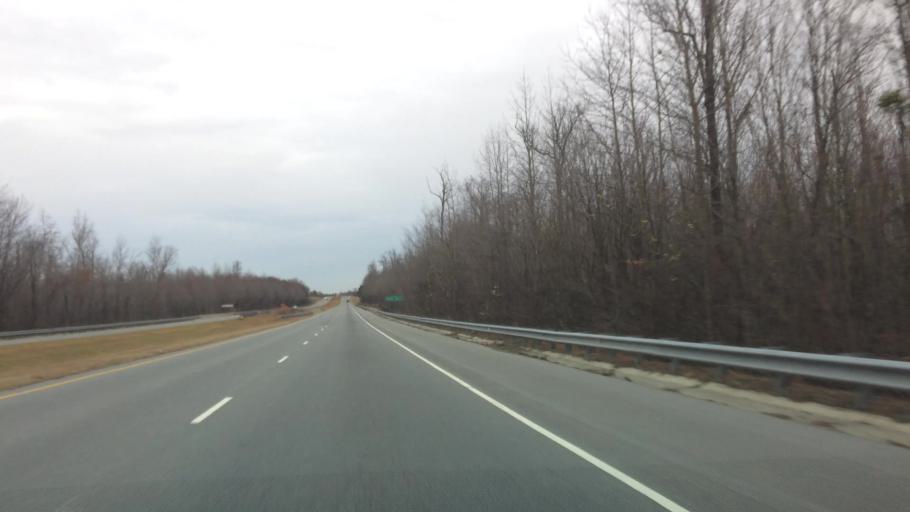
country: US
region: North Carolina
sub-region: Wayne County
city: Mount Olive
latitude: 35.1443
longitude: -78.1278
